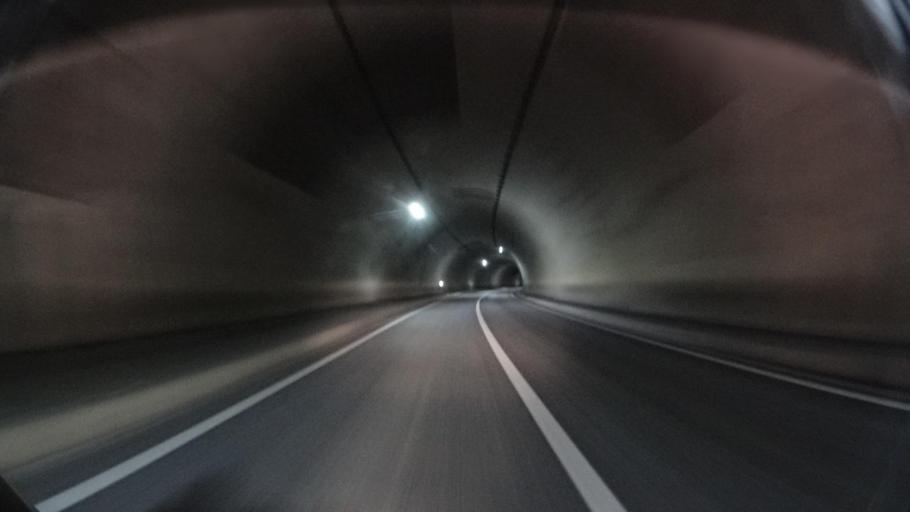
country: JP
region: Kyoto
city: Maizuru
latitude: 35.5224
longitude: 135.3501
